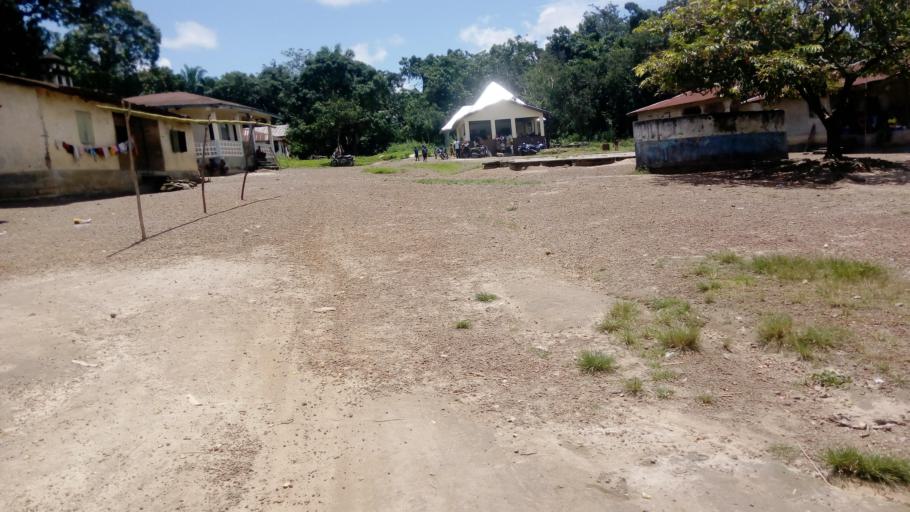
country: SL
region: Northern Province
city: Binkolo
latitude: 8.9184
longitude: -12.0068
